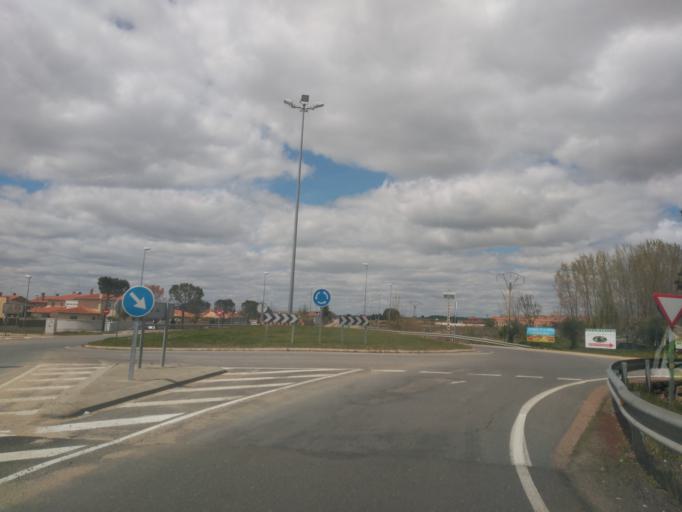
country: ES
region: Castille and Leon
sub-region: Provincia de Salamanca
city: Villamayor
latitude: 41.0090
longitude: -5.7069
